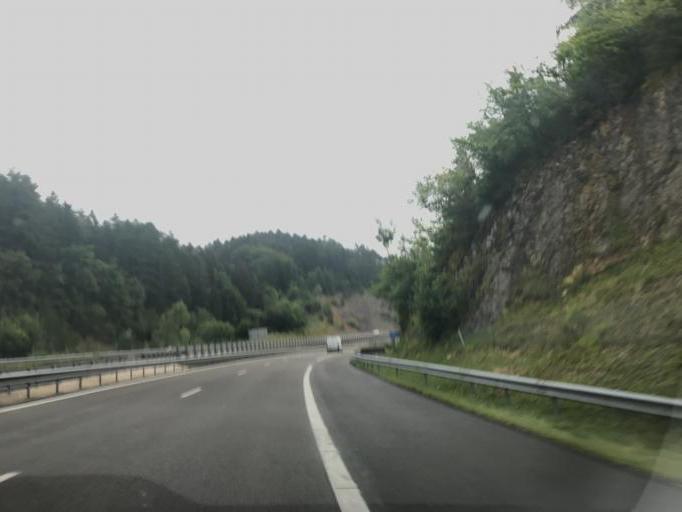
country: FR
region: Rhone-Alpes
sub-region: Departement de l'Ain
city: Montreal-la-Cluse
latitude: 46.1878
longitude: 5.5670
